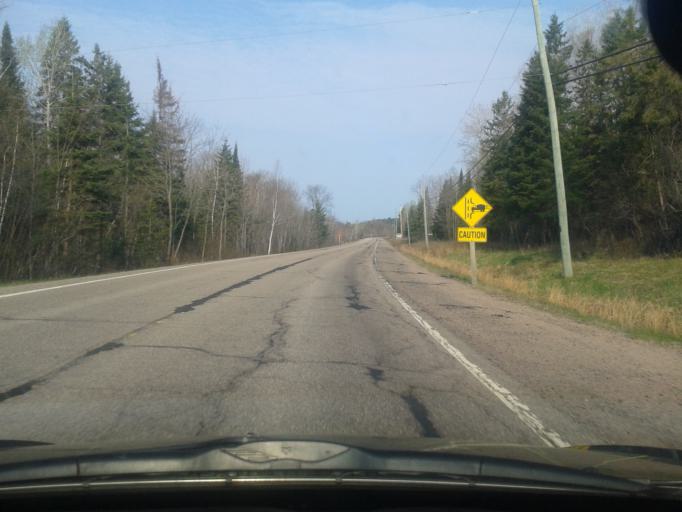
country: CA
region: Ontario
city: Powassan
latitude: 46.1927
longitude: -79.3468
